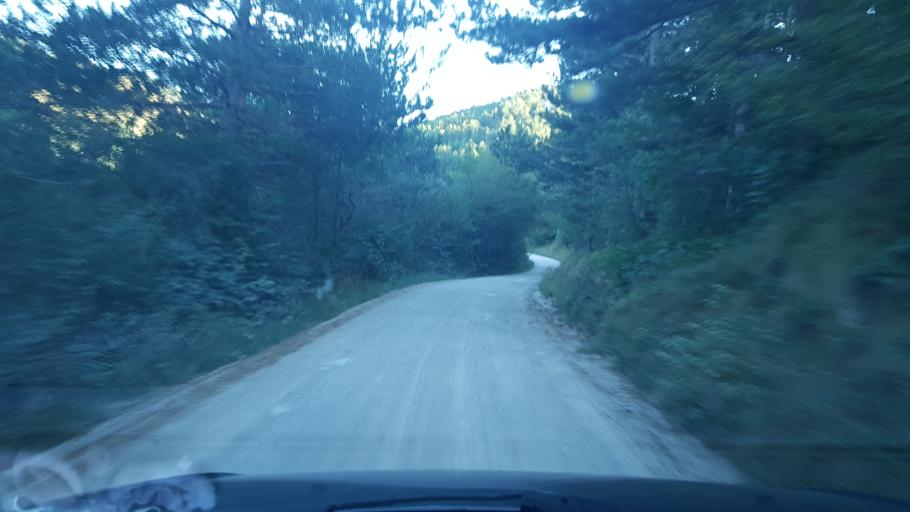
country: SI
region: Vipava
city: Vipava
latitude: 45.7952
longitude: 14.0155
